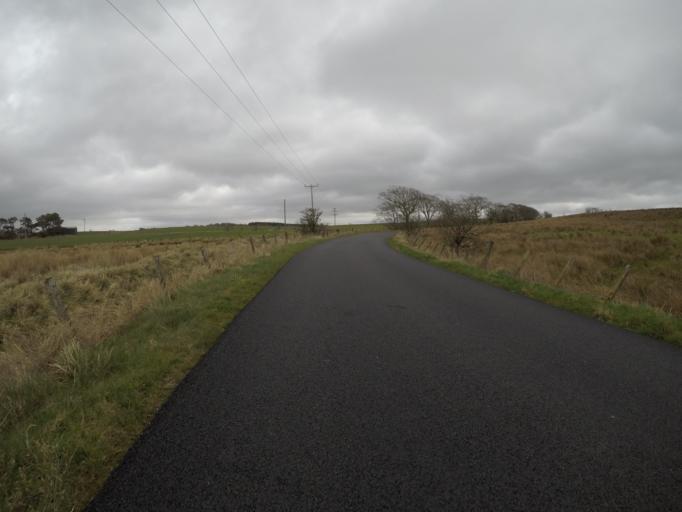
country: GB
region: Scotland
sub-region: East Ayrshire
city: Stewarton
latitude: 55.6822
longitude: -4.4616
